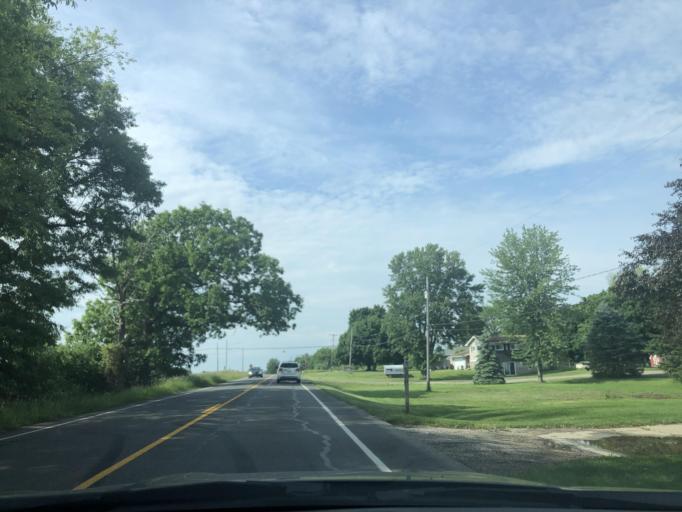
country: US
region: Michigan
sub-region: Clinton County
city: Bath
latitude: 42.8115
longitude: -84.4837
